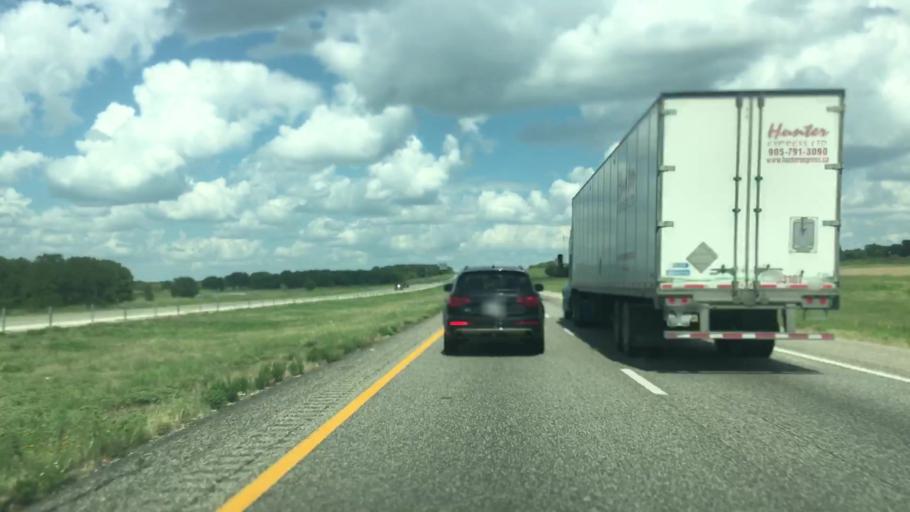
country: US
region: Texas
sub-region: Hill County
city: Hillsboro
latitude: 32.0597
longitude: -97.0870
